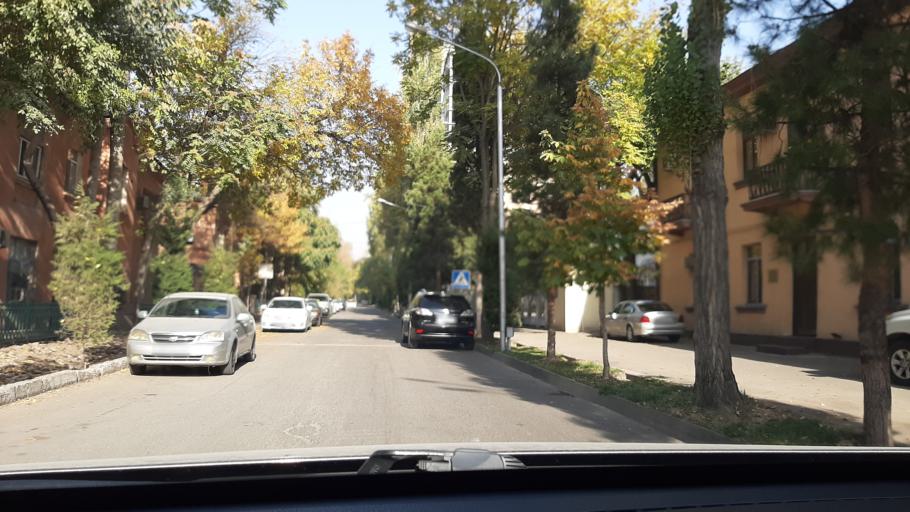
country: TJ
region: Dushanbe
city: Dushanbe
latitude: 38.5639
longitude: 68.7943
